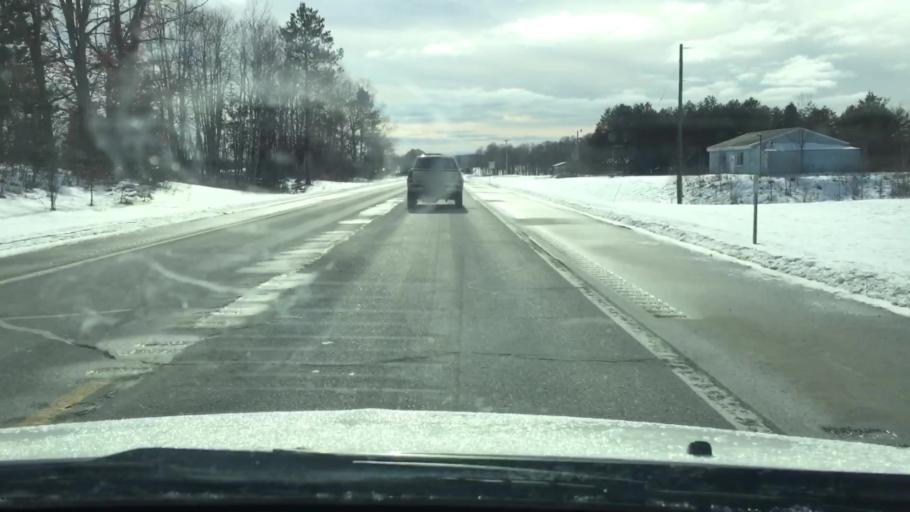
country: US
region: Michigan
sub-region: Wexford County
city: Manton
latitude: 44.6003
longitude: -85.3285
